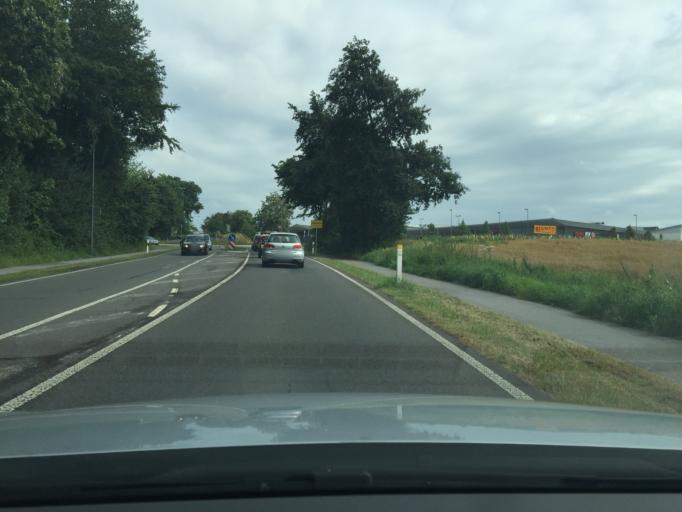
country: DE
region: North Rhine-Westphalia
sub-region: Regierungsbezirk Dusseldorf
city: Heiligenhaus
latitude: 51.3266
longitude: 6.9420
